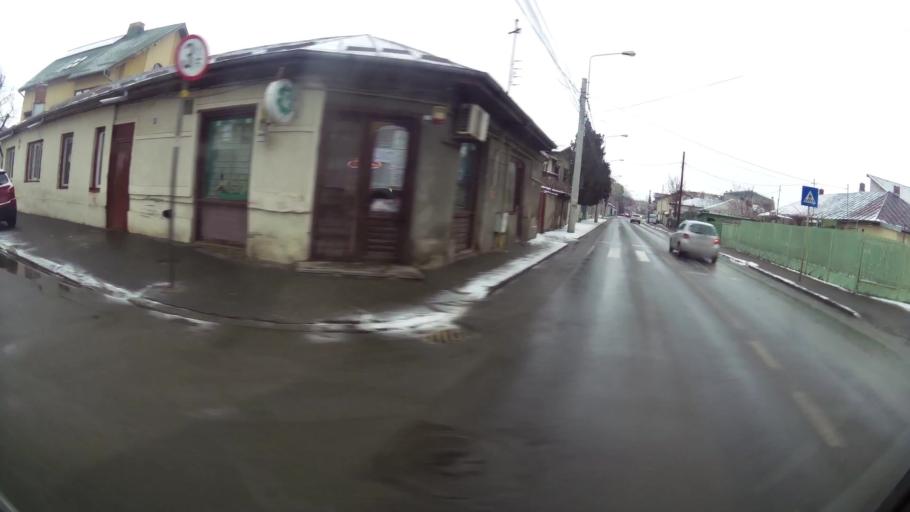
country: RO
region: Prahova
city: Ploiesti
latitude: 44.9365
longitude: 26.0423
